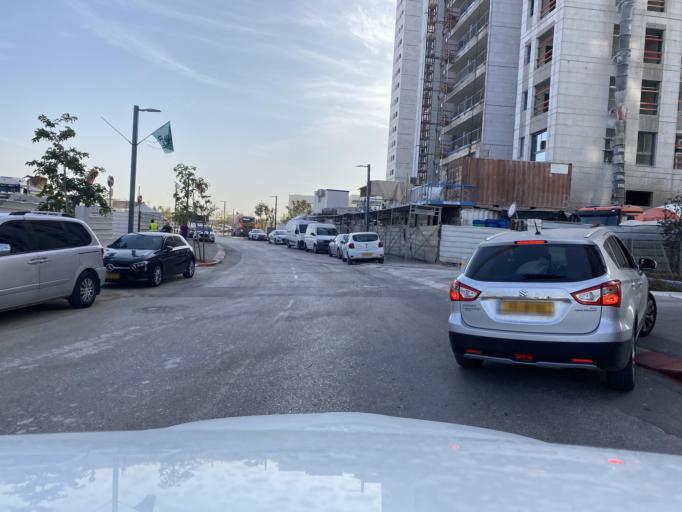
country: IL
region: Tel Aviv
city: Giv`at Shemu'el
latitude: 32.0713
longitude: 34.8517
